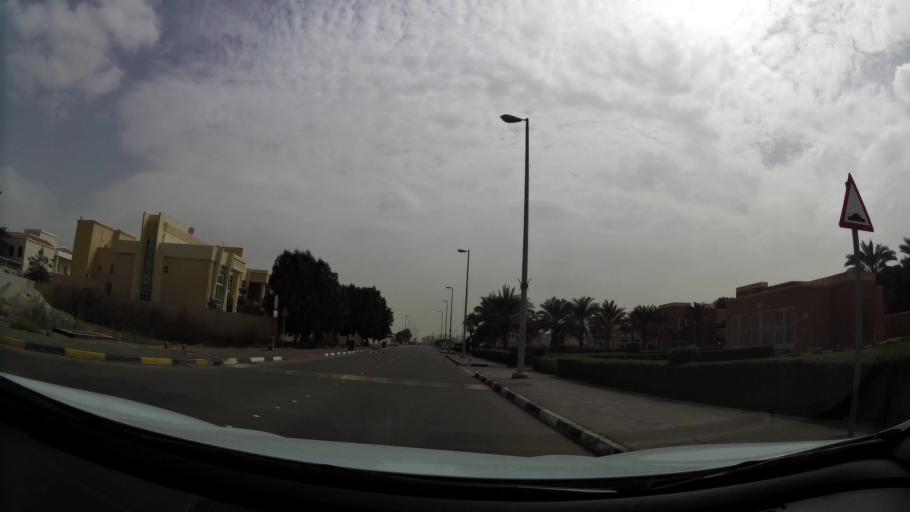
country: AE
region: Abu Dhabi
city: Abu Dhabi
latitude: 24.3934
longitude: 54.4951
